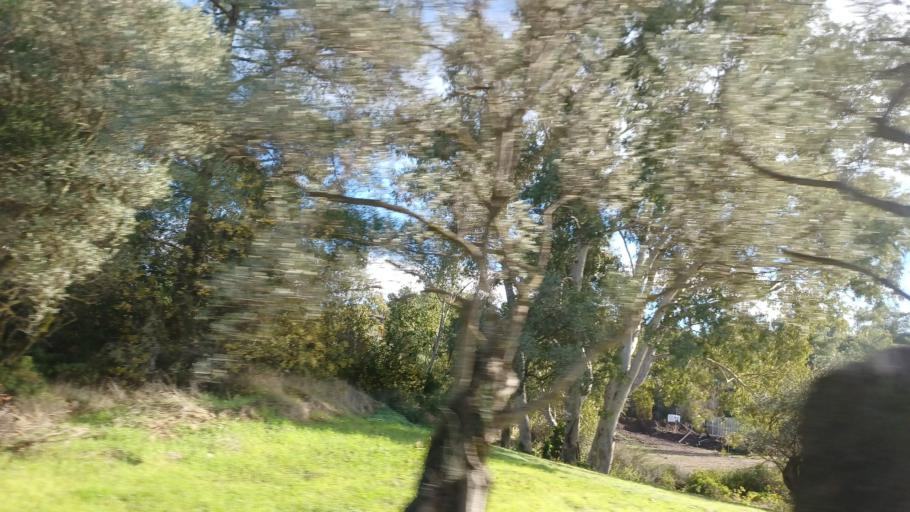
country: CY
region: Lefkosia
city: Lythrodontas
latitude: 34.9355
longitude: 33.2978
